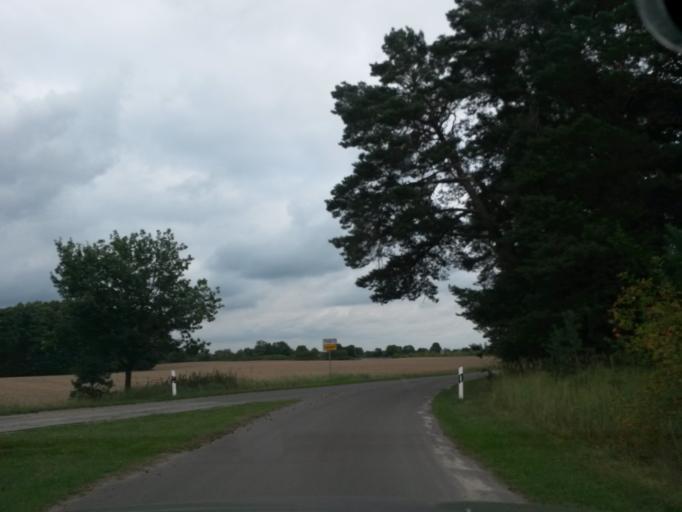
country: DE
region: Brandenburg
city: Gerswalde
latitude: 53.0940
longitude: 13.8470
